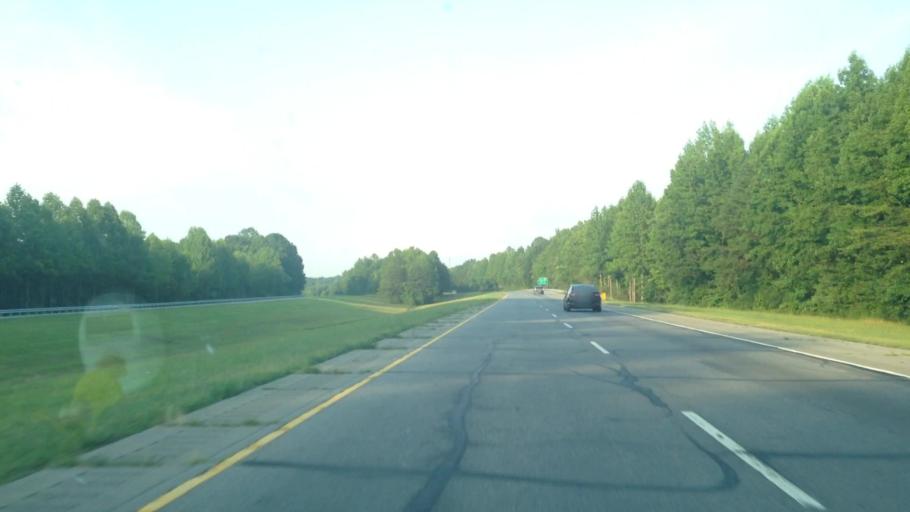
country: US
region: Virginia
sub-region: City of Danville
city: Danville
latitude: 36.4744
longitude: -79.5111
